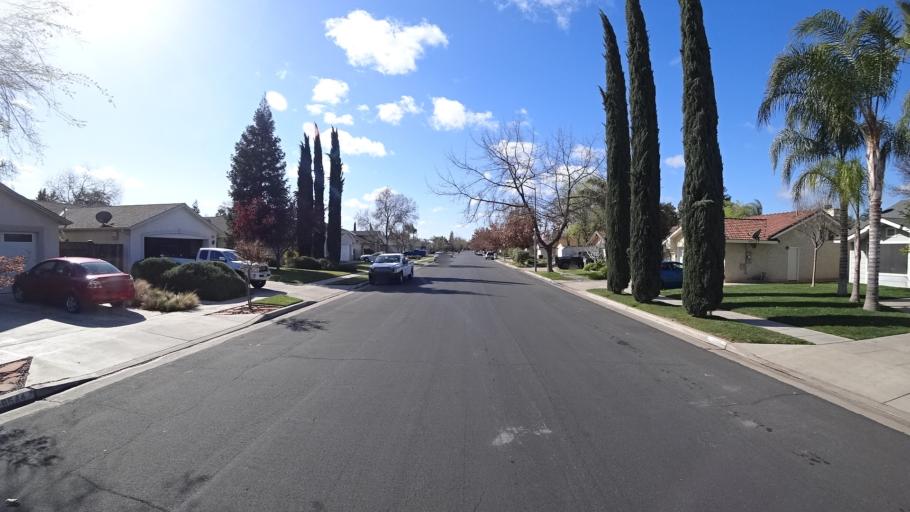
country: US
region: California
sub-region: Fresno County
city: West Park
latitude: 36.8324
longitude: -119.8807
